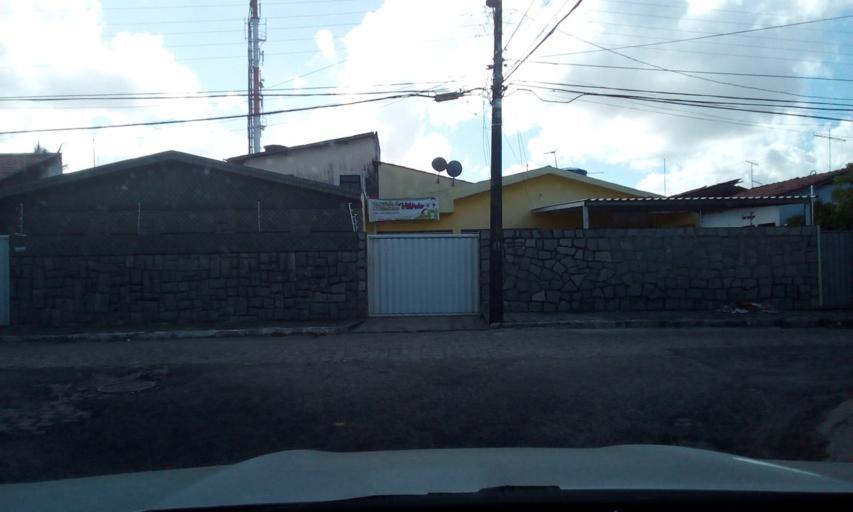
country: BR
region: Paraiba
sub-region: Joao Pessoa
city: Joao Pessoa
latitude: -7.1750
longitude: -34.8391
